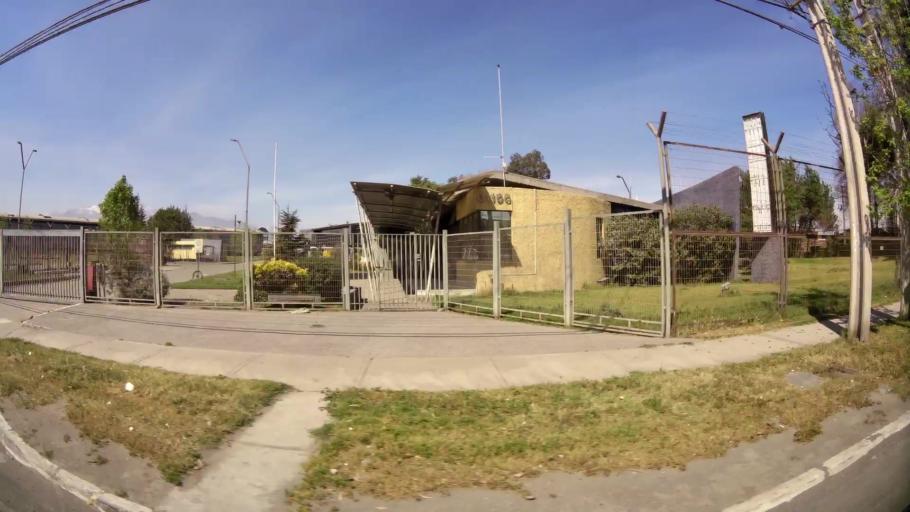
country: CL
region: Santiago Metropolitan
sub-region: Provincia de Maipo
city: San Bernardo
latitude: -33.5467
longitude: -70.6989
